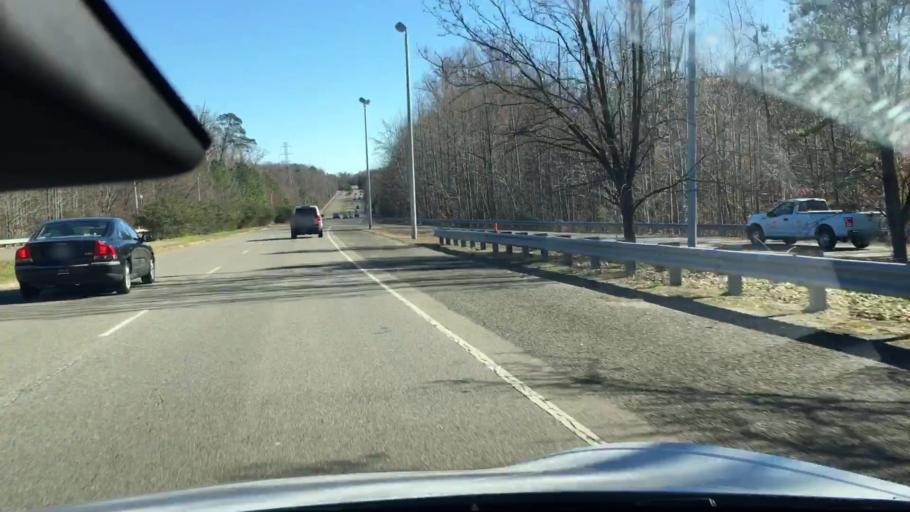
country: US
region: Virginia
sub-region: Chesterfield County
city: Bon Air
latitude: 37.5499
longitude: -77.5665
